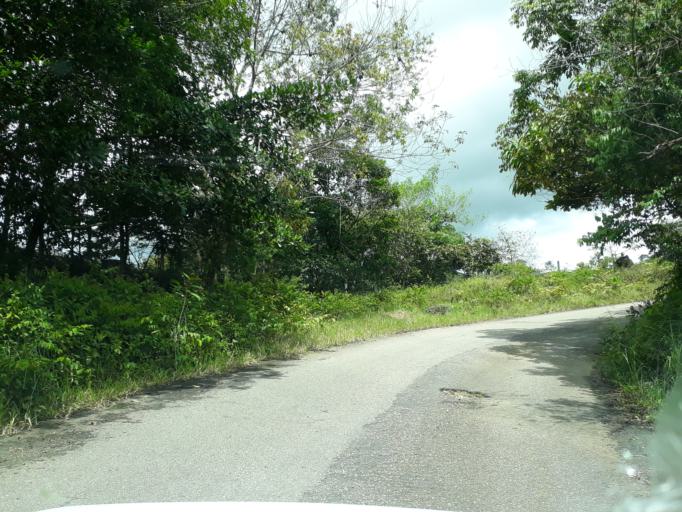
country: CO
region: Cundinamarca
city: Medina
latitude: 4.5787
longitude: -73.3429
